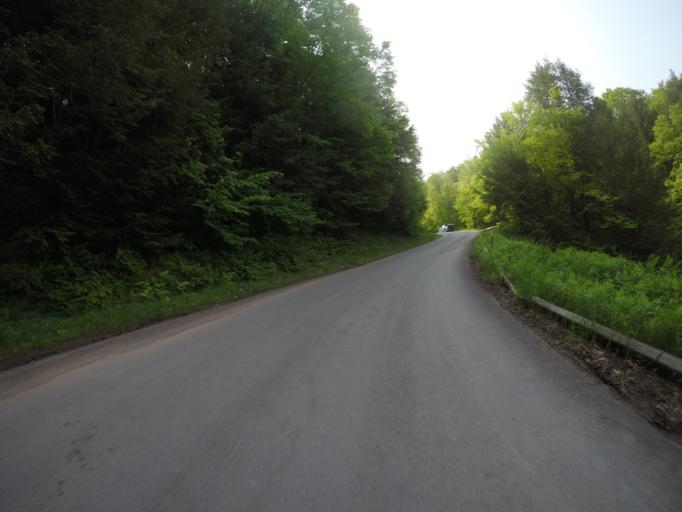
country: US
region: New York
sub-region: Sullivan County
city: Livingston Manor
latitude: 42.0760
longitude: -74.7648
